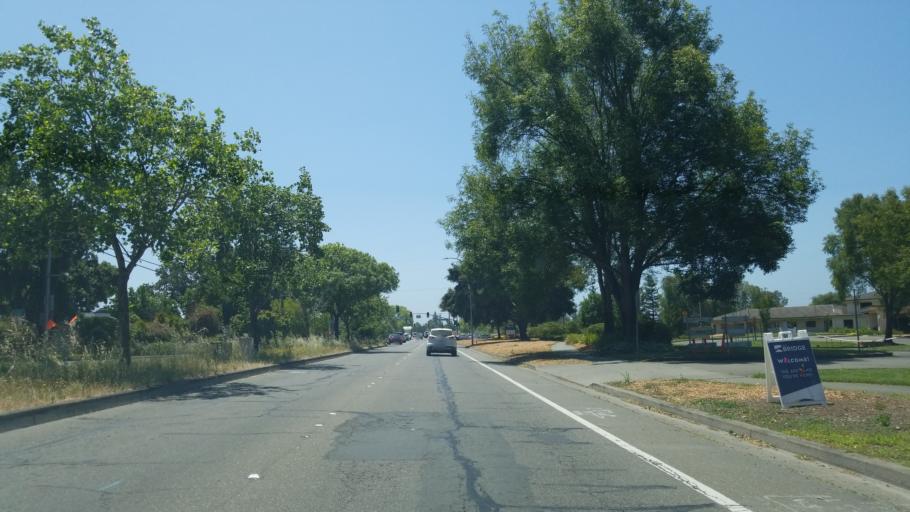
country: US
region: California
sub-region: Sonoma County
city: Roseland
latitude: 38.4305
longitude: -122.7697
